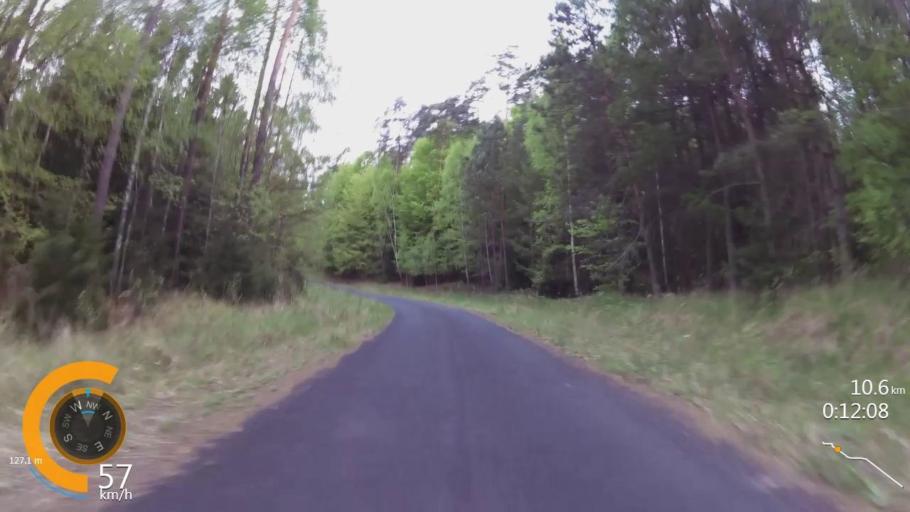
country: PL
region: West Pomeranian Voivodeship
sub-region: Powiat drawski
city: Wierzchowo
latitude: 53.5185
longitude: 16.1068
